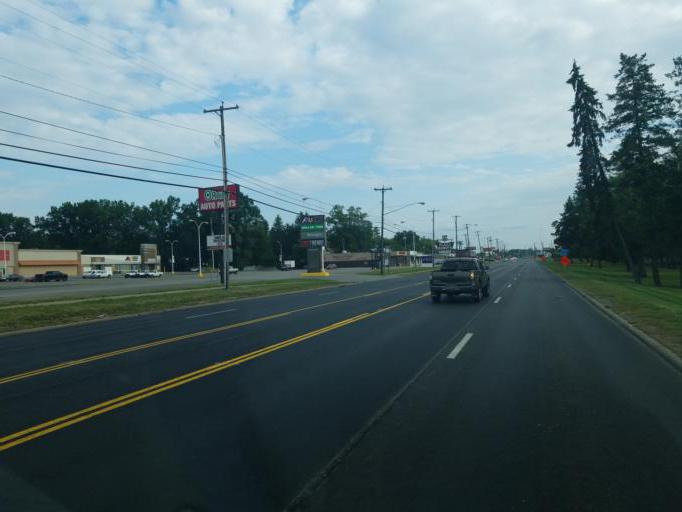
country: US
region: Ohio
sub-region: Trumbull County
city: Churchill
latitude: 41.1452
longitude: -80.6655
